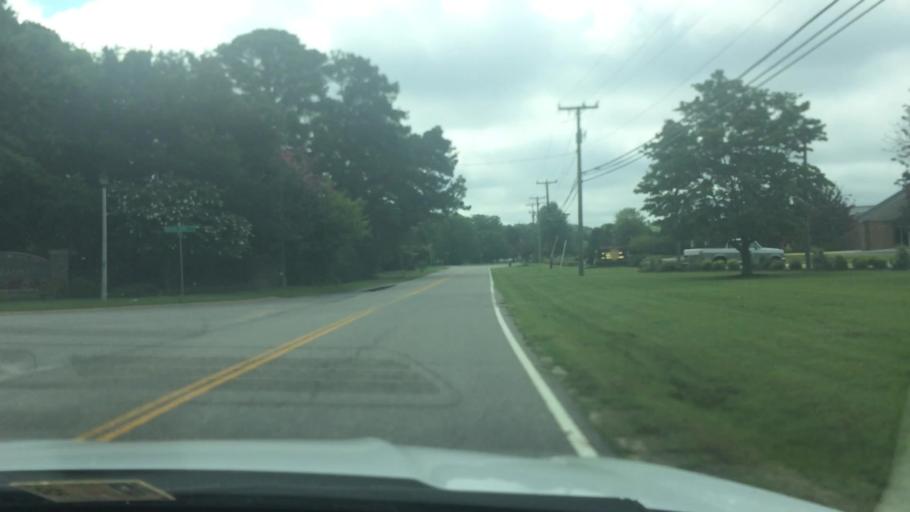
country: US
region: Virginia
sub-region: City of Poquoson
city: Poquoson
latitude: 37.1277
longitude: -76.4372
